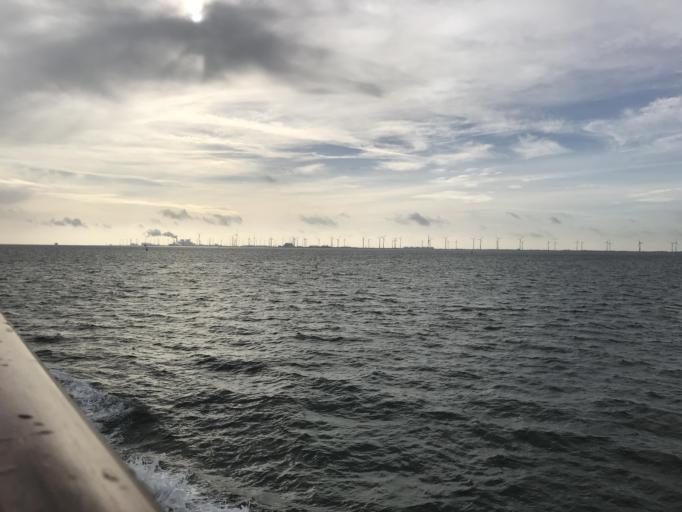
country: DE
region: Lower Saxony
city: Borkum
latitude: 53.5136
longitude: 6.7922
